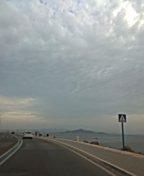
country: ES
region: Murcia
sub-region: Murcia
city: La Manga del Mar Menor
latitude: 37.7258
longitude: -0.7405
